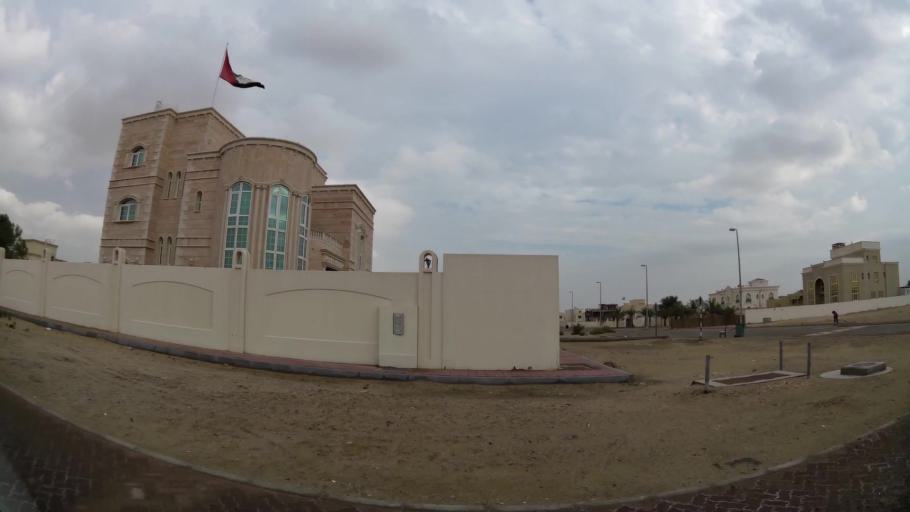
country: AE
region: Abu Dhabi
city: Abu Dhabi
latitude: 24.3431
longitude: 54.6185
